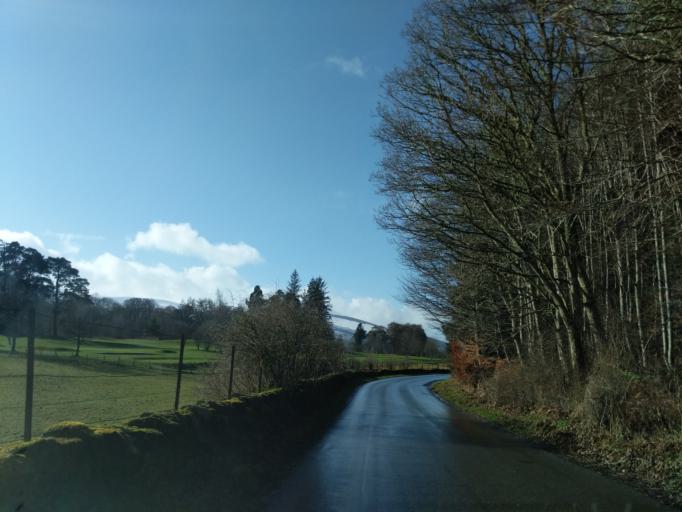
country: GB
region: Scotland
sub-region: Perth and Kinross
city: Aberfeldy
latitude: 56.5932
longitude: -3.9925
